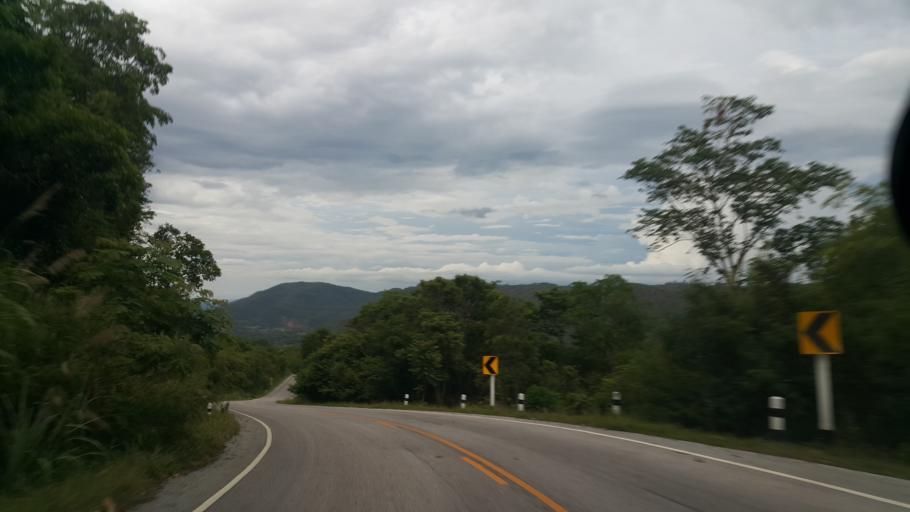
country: TH
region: Loei
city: Na Haeo
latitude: 17.4857
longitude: 101.1755
